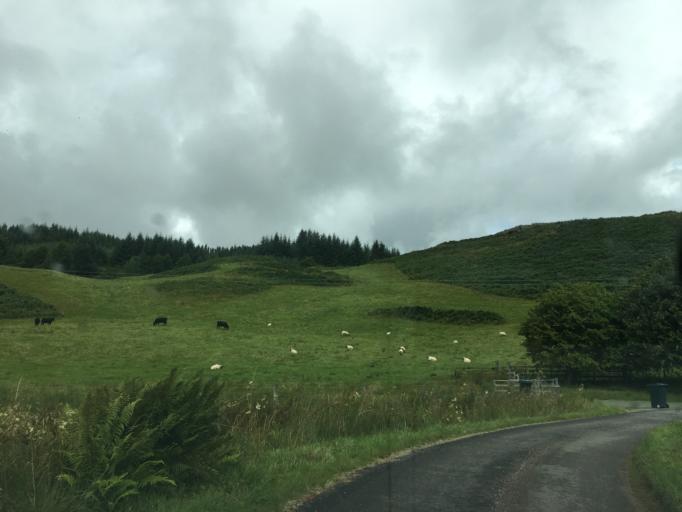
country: GB
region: Scotland
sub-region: Argyll and Bute
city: Oban
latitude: 56.2585
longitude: -5.3985
